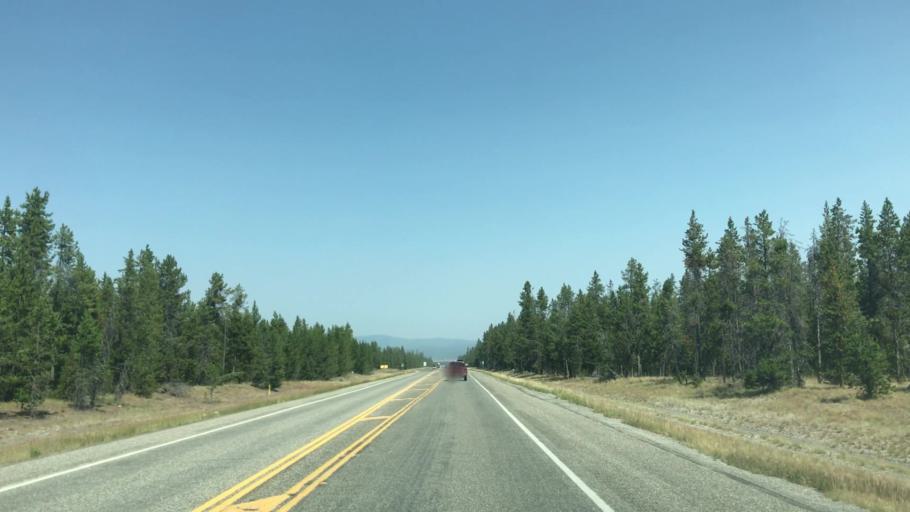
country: US
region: Montana
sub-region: Gallatin County
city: West Yellowstone
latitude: 44.6840
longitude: -111.1010
